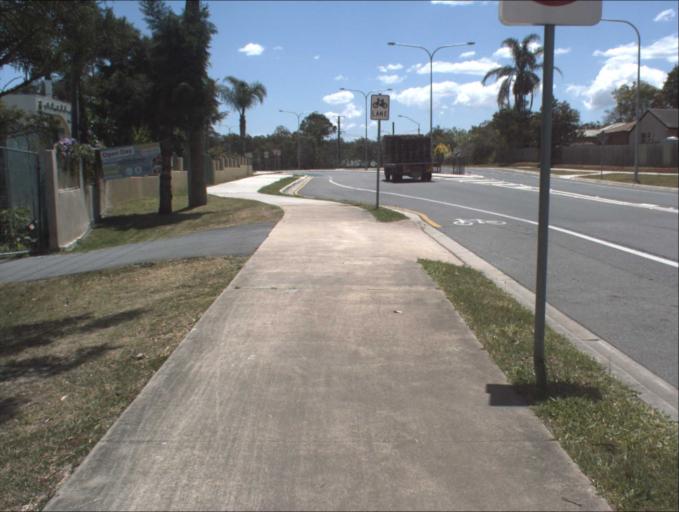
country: AU
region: Queensland
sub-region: Logan
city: Logan City
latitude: -27.6591
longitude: 153.0917
